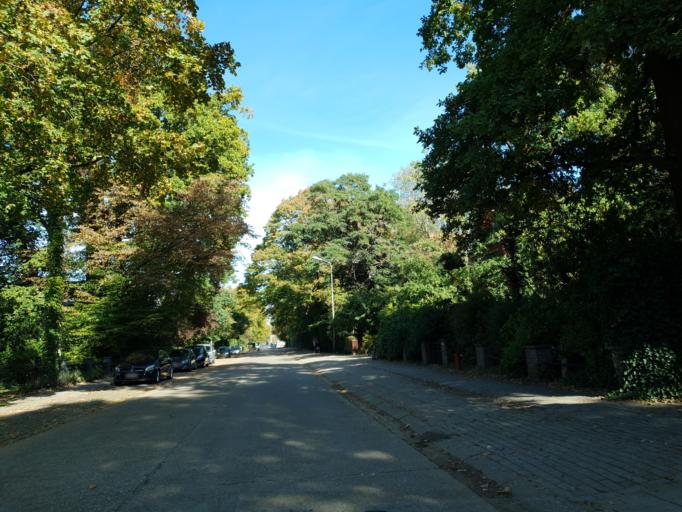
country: BE
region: Flanders
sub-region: Provincie Antwerpen
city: Kapellen
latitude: 51.2862
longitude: 4.4392
